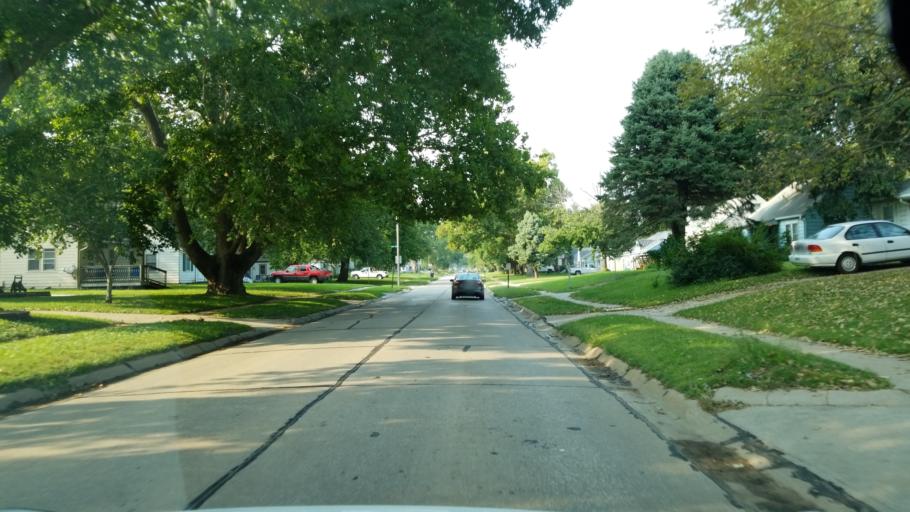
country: US
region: Nebraska
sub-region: Sarpy County
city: Bellevue
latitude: 41.1316
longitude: -95.8924
